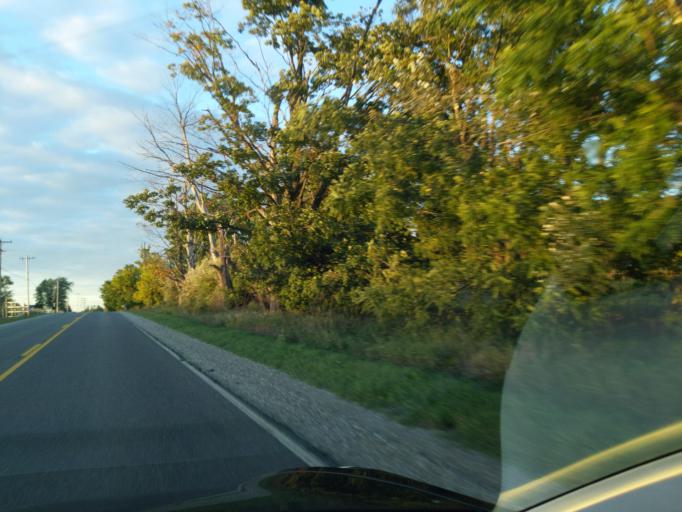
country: US
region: Michigan
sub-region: Antrim County
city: Elk Rapids
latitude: 44.8229
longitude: -85.4049
